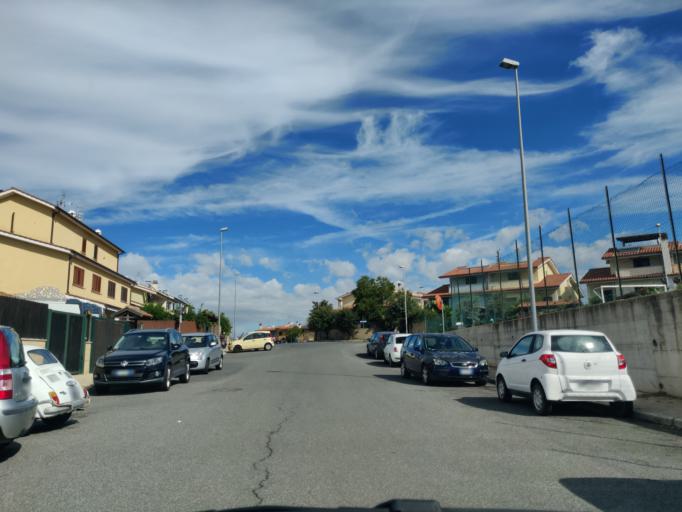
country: IT
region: Latium
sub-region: Citta metropolitana di Roma Capitale
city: Civitavecchia
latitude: 42.0632
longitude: 11.8185
